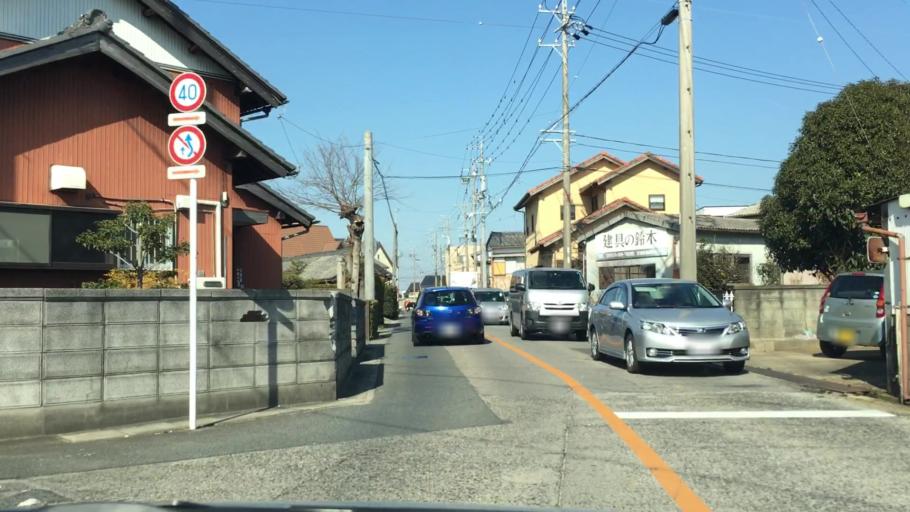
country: JP
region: Aichi
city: Anjo
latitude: 34.9730
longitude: 137.1204
